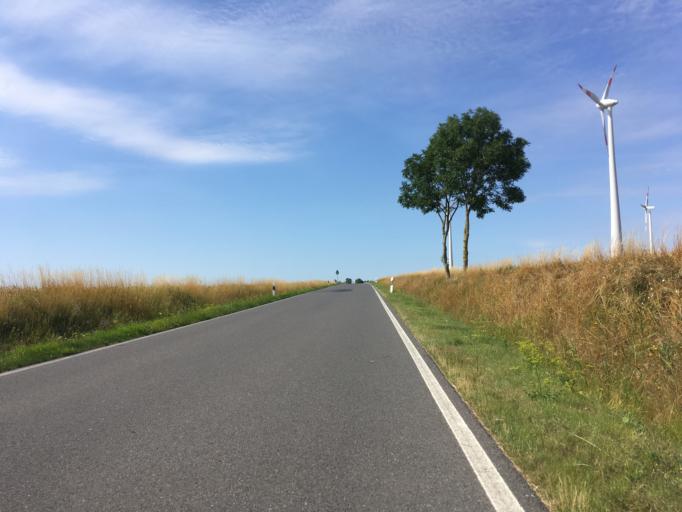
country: DE
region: Brandenburg
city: Gramzow
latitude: 53.2569
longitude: 14.0618
